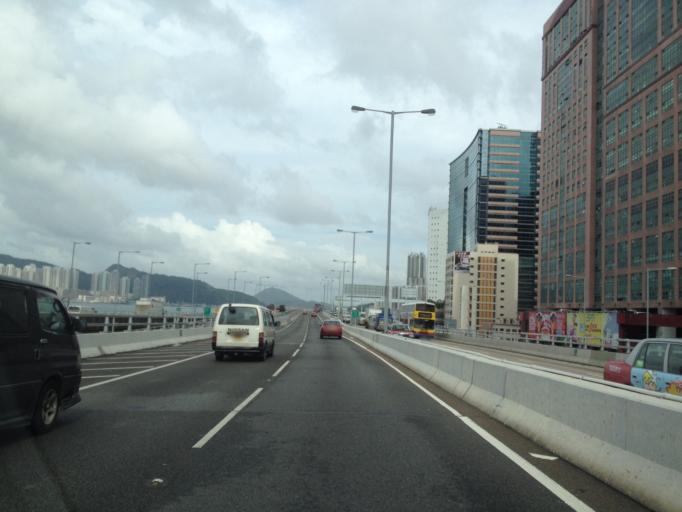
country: HK
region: Kowloon City
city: Kowloon
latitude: 22.2938
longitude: 114.2058
